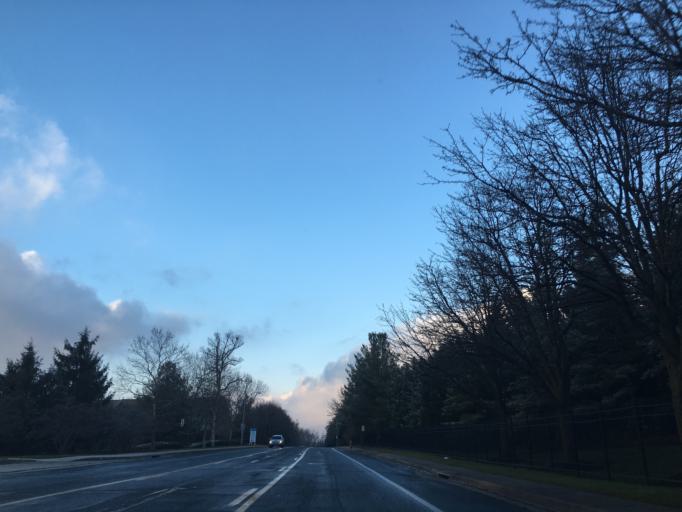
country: US
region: Maryland
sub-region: Baltimore County
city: Pikesville
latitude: 39.3906
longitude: -76.7353
